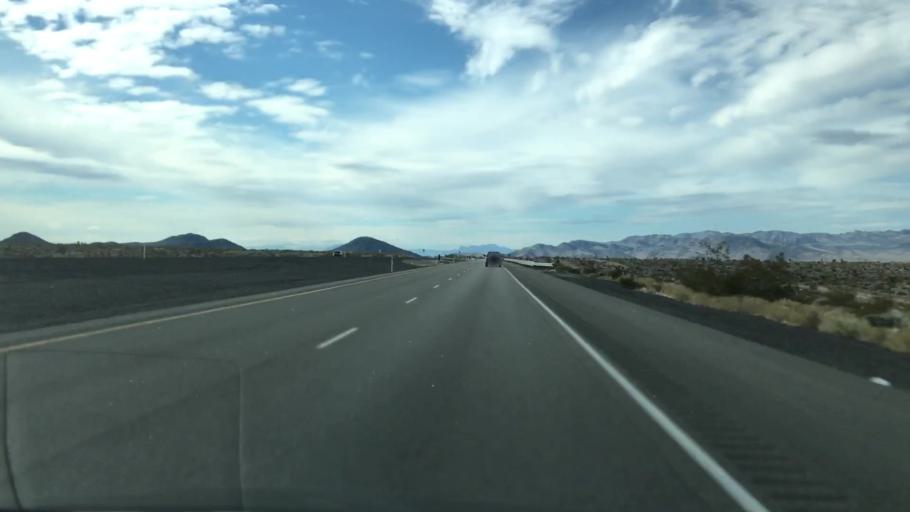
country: US
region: Nevada
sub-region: Nye County
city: Pahrump
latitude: 36.6012
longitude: -115.9869
